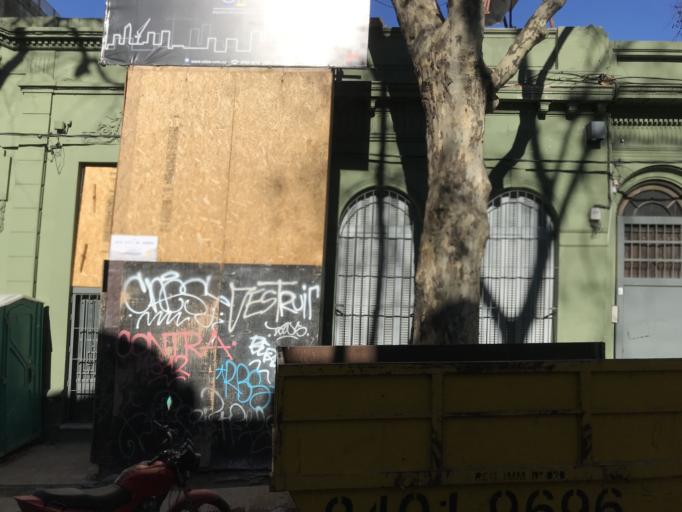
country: UY
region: Montevideo
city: Montevideo
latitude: -34.9001
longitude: -56.1792
